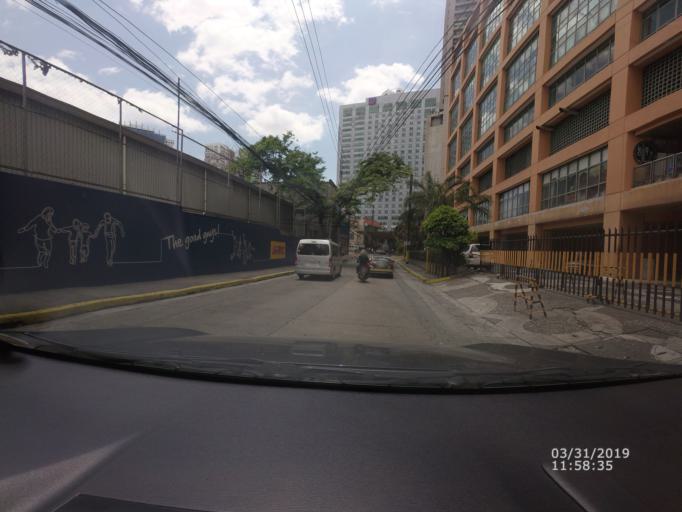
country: PH
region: Metro Manila
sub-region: Mandaluyong
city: Mandaluyong City
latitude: 14.5725
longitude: 121.0502
